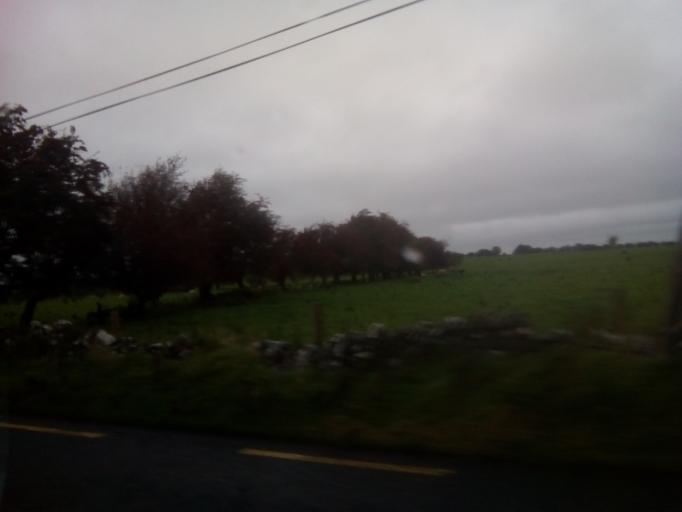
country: IE
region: Connaught
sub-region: Roscommon
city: Roscommon
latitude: 53.7693
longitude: -8.2213
